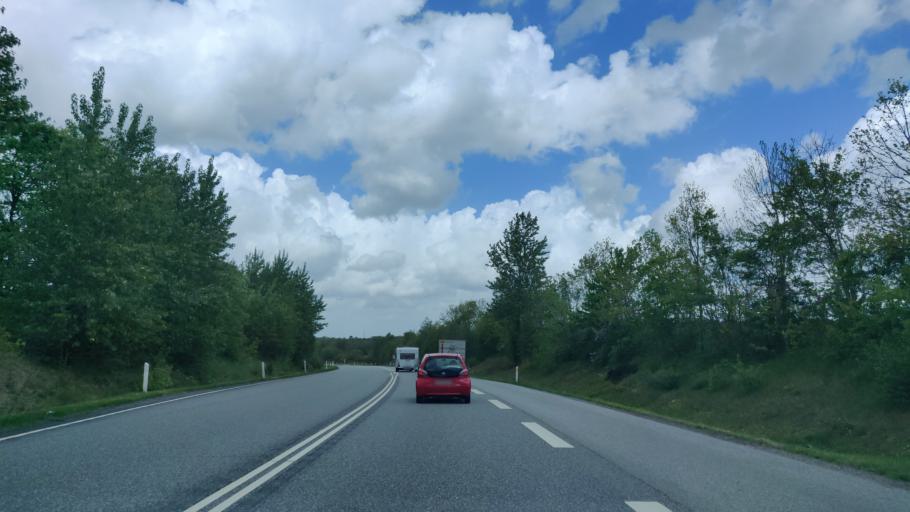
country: DK
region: Central Jutland
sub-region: Hedensted Kommune
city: Torring
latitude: 55.9654
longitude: 9.4054
